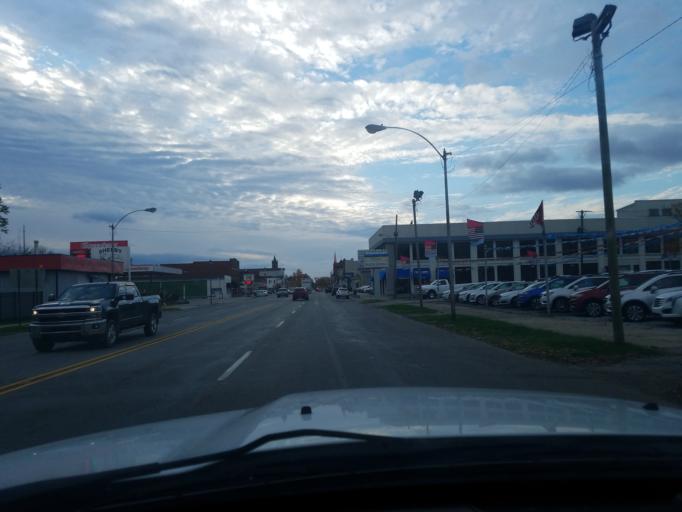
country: US
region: Indiana
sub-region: Shelby County
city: Shelbyville
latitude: 39.5230
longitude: -85.7742
